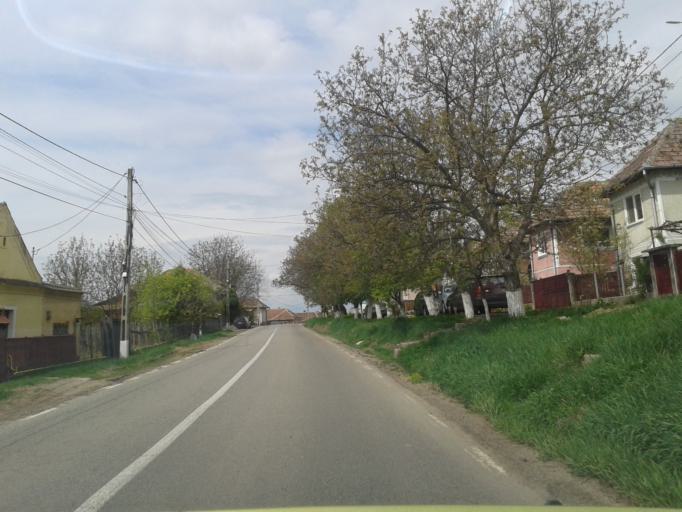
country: RO
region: Alba
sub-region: Comuna Valea Lunga
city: Valea Lunga
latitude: 46.1222
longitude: 24.0315
